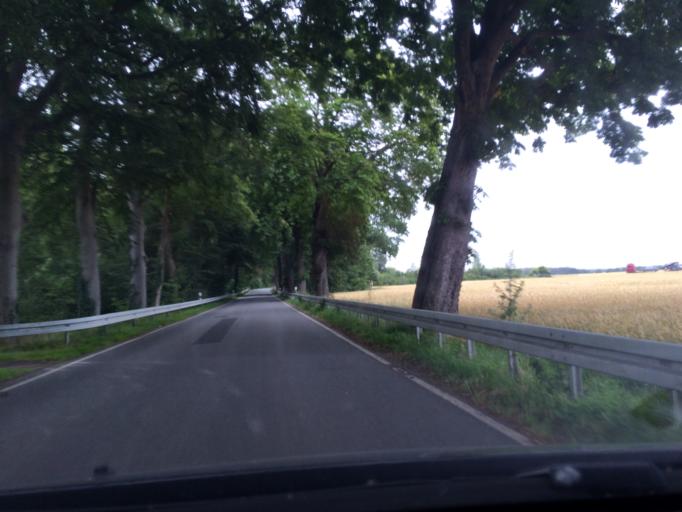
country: DE
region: Mecklenburg-Vorpommern
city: Altenpleen
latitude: 54.3968
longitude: 12.9736
